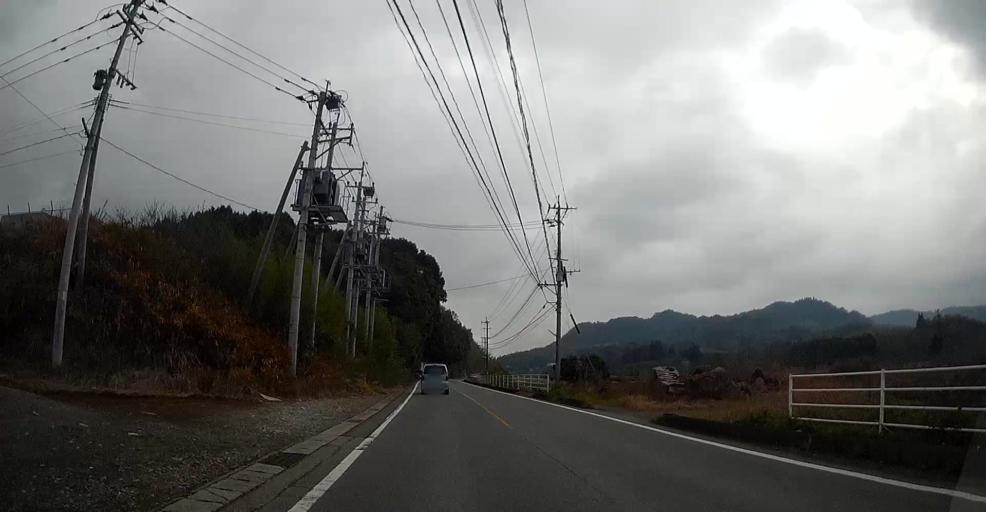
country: JP
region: Kumamoto
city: Matsubase
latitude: 32.6481
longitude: 130.7211
